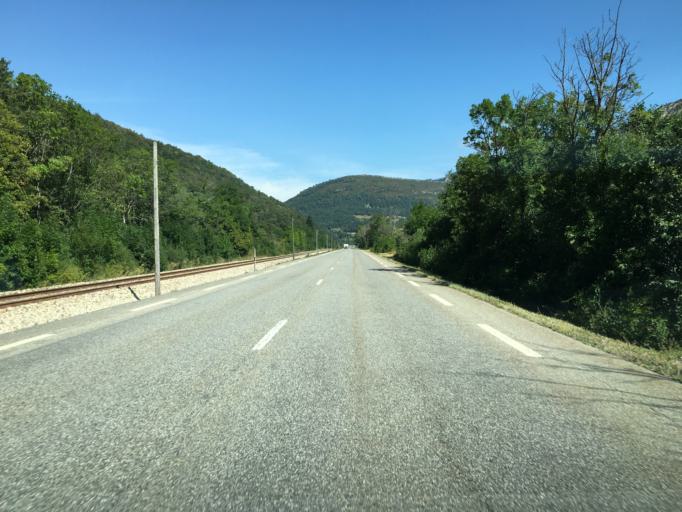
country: FR
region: Provence-Alpes-Cote d'Azur
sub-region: Departement des Hautes-Alpes
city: Veynes
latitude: 44.6031
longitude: 5.7087
